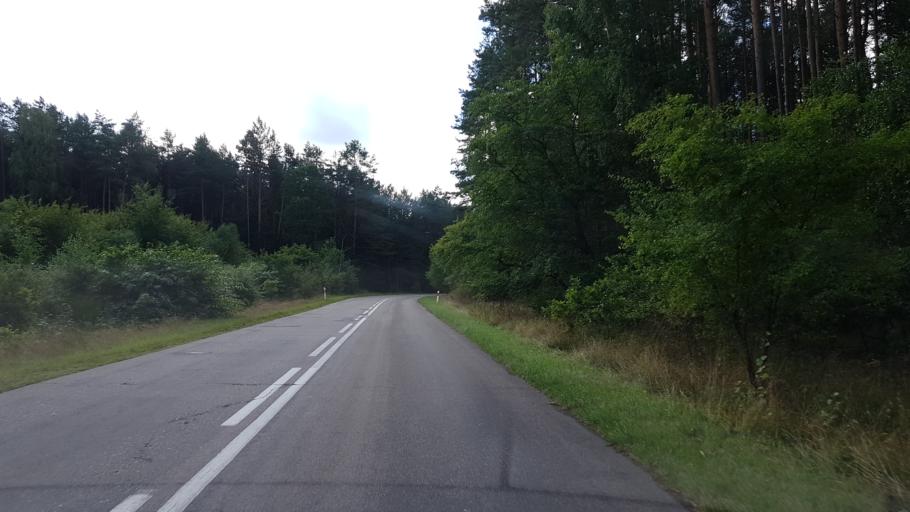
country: PL
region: West Pomeranian Voivodeship
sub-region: Powiat bialogardzki
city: Tychowo
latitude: 54.0572
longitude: 16.3020
